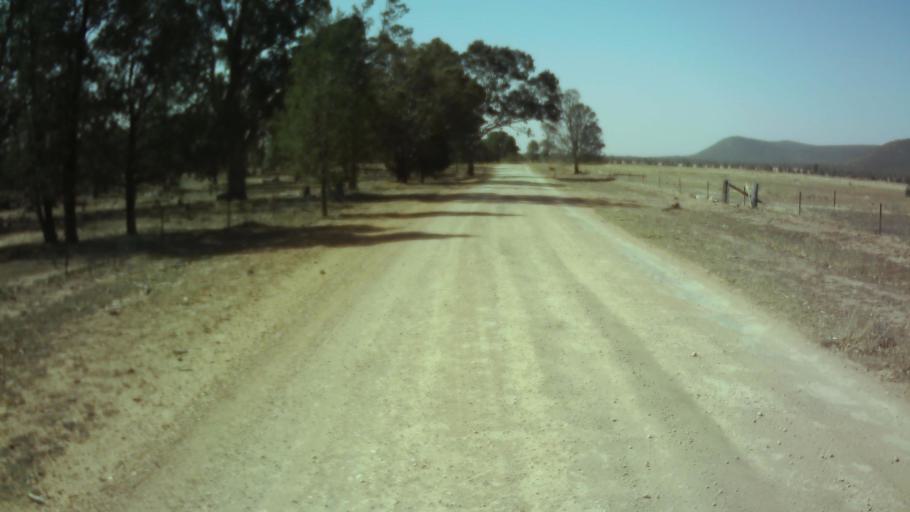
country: AU
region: New South Wales
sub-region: Weddin
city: Grenfell
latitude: -33.9474
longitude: 147.9281
